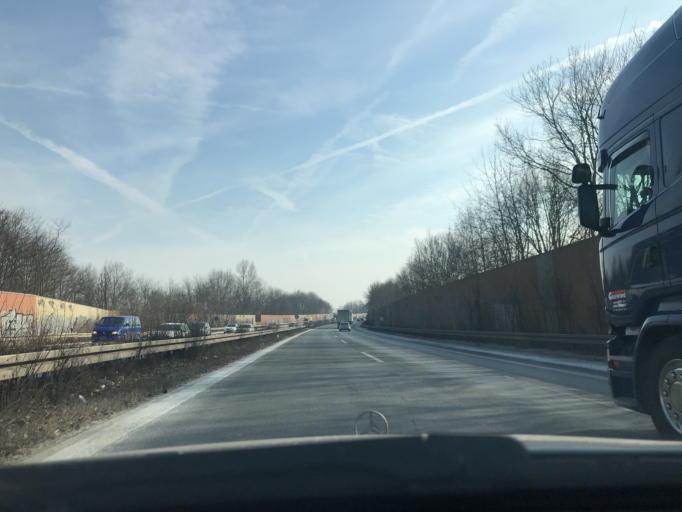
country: DE
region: North Rhine-Westphalia
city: Lanstrop
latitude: 51.5591
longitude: 7.5112
